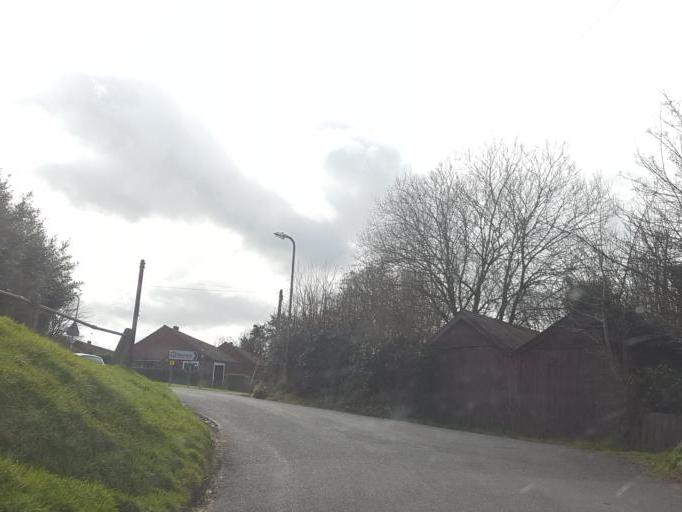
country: GB
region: England
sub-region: Worcestershire
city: Great Malvern
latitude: 52.1209
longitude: -2.3463
